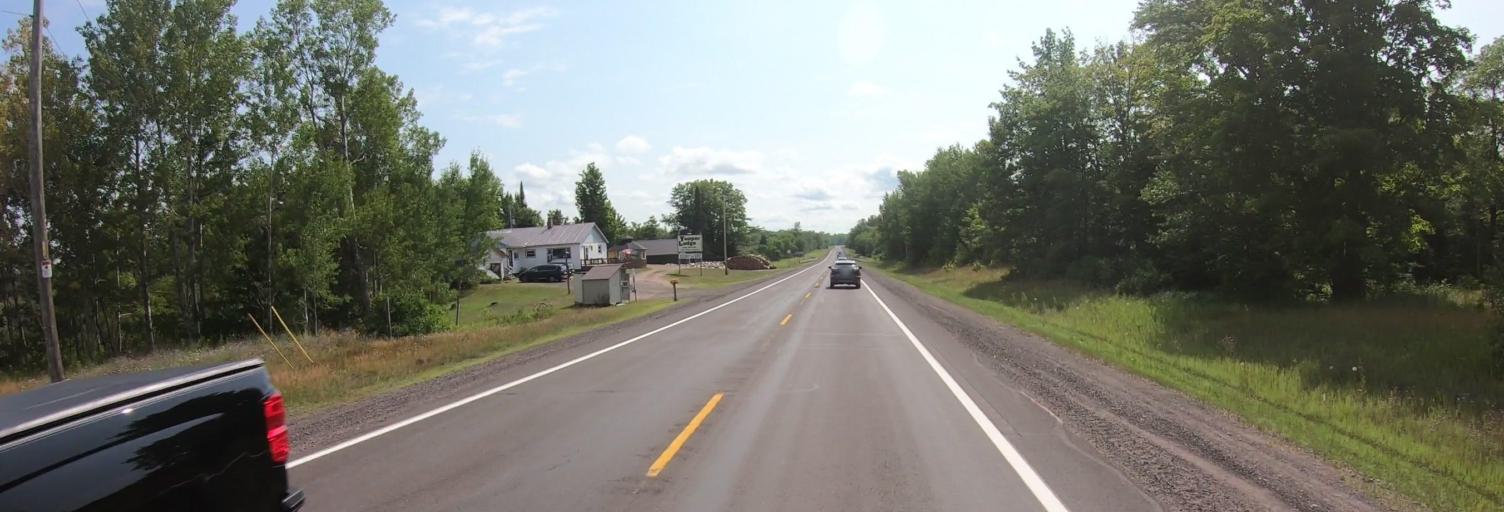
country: US
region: Michigan
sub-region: Houghton County
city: Hancock
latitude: 46.8844
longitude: -88.8639
